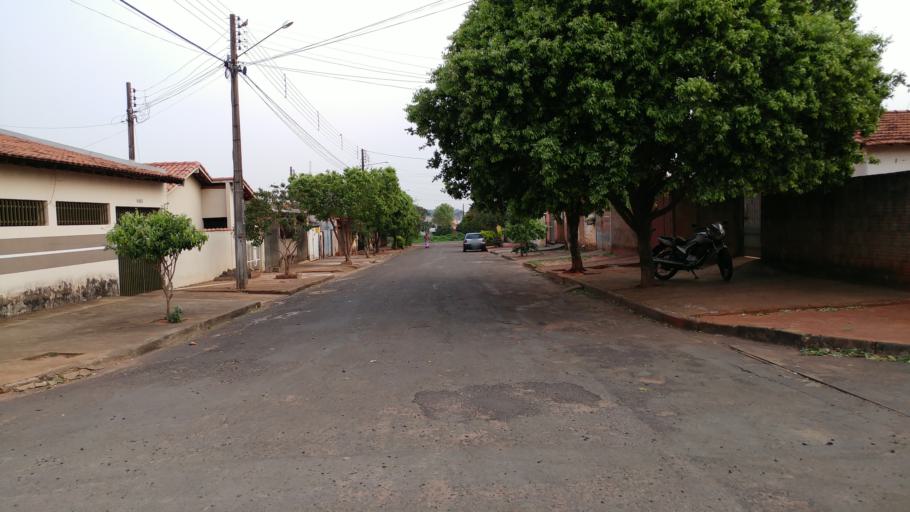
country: BR
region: Sao Paulo
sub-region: Paraguacu Paulista
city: Paraguacu Paulista
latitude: -22.4358
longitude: -50.5818
